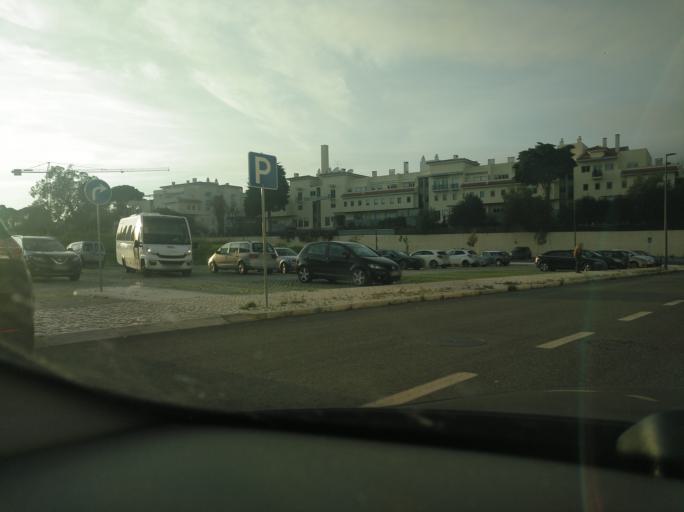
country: PT
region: Lisbon
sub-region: Odivelas
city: Olival do Basto
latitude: 38.7722
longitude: -9.1696
